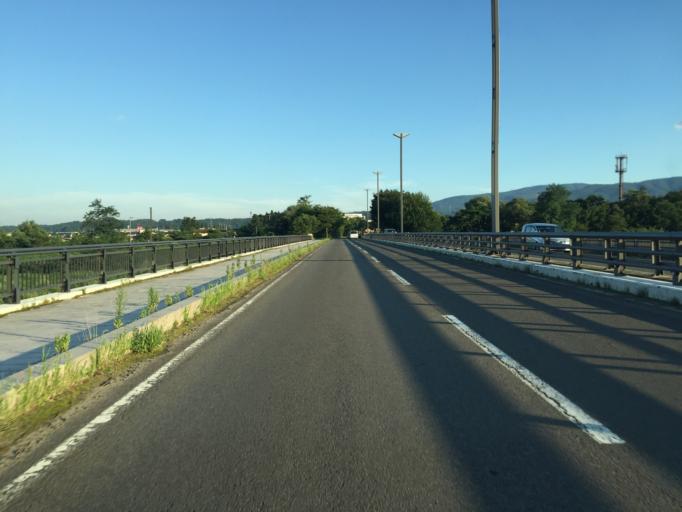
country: JP
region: Fukushima
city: Fukushima-shi
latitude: 37.7349
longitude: 140.3854
